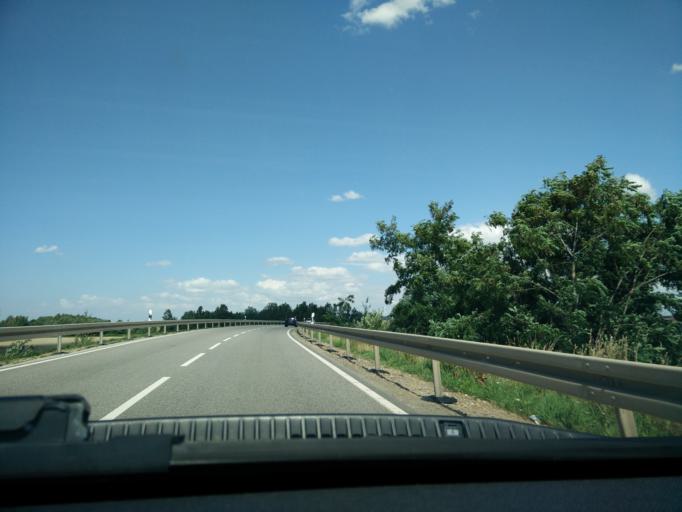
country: DE
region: Saxony
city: Penig
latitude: 50.9548
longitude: 12.6870
